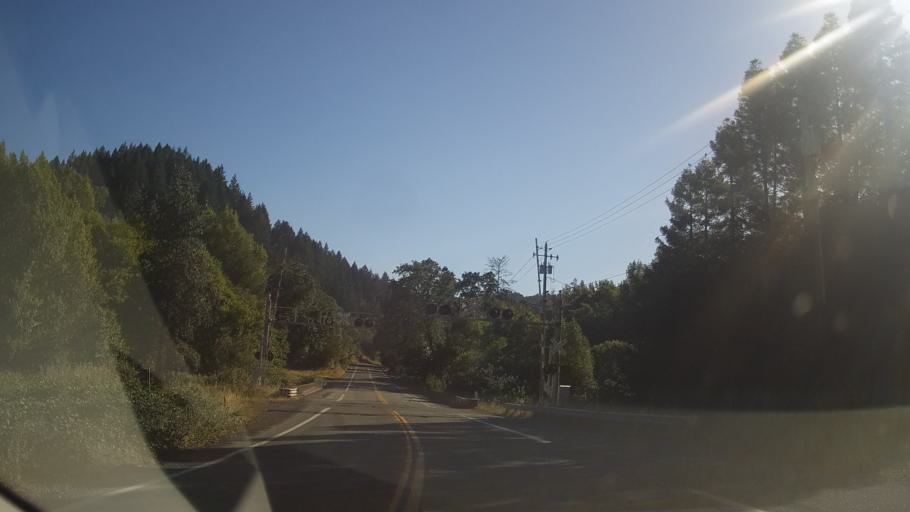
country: US
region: California
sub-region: Mendocino County
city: Willits
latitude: 39.4077
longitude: -123.3789
